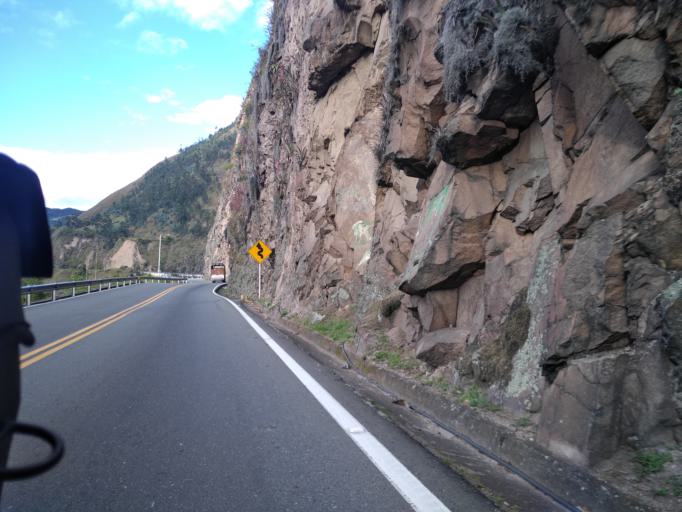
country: CO
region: Narino
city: Funes
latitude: 0.9518
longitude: -77.4711
